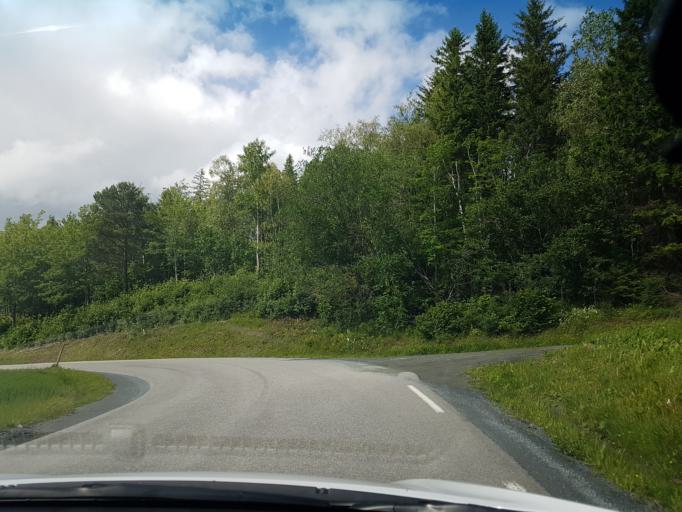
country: NO
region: Nord-Trondelag
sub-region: Stjordal
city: Stjordalshalsen
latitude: 63.5902
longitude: 11.0063
